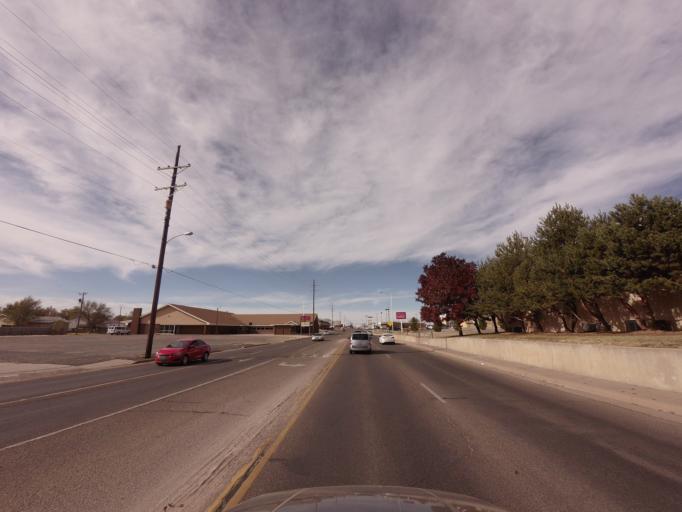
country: US
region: New Mexico
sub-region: Curry County
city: Clovis
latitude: 34.4193
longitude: -103.2101
